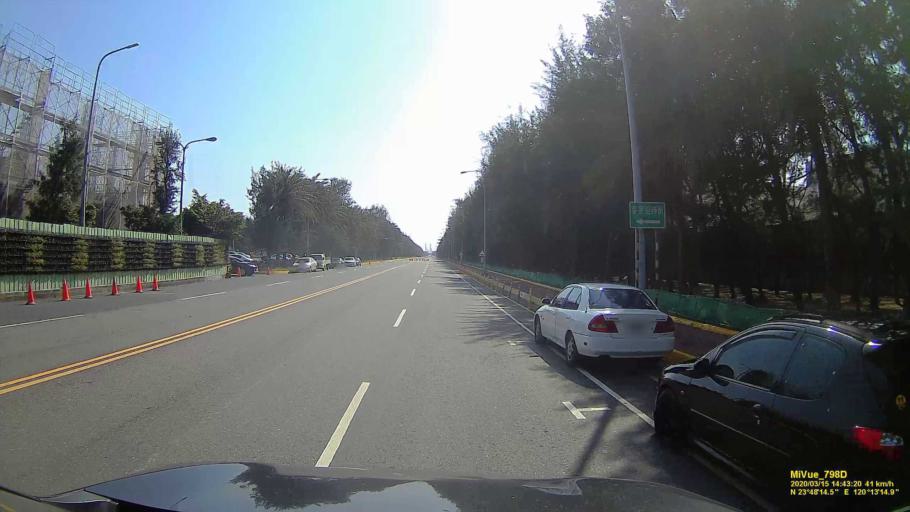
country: TW
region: Taiwan
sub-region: Yunlin
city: Douliu
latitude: 23.8039
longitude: 120.2206
